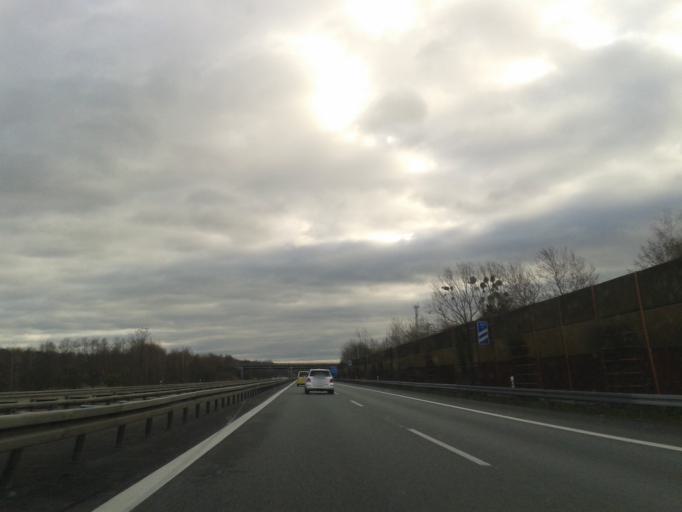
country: DE
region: Saxony
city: Lichtenberg
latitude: 51.1591
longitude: 13.9694
